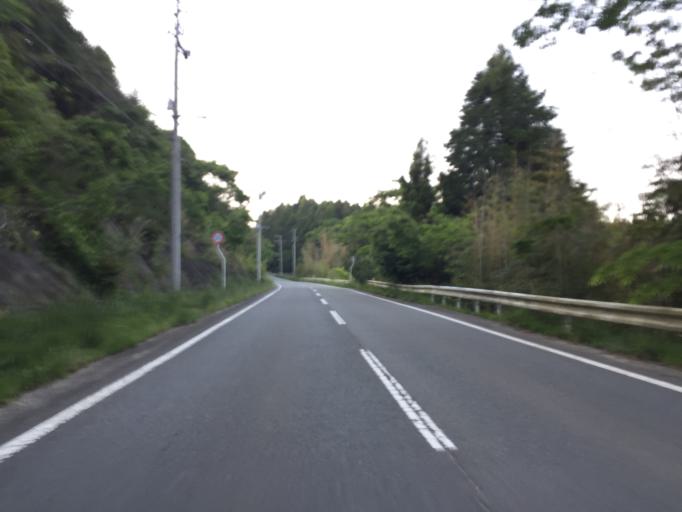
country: JP
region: Fukushima
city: Namie
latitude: 37.2696
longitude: 140.9762
